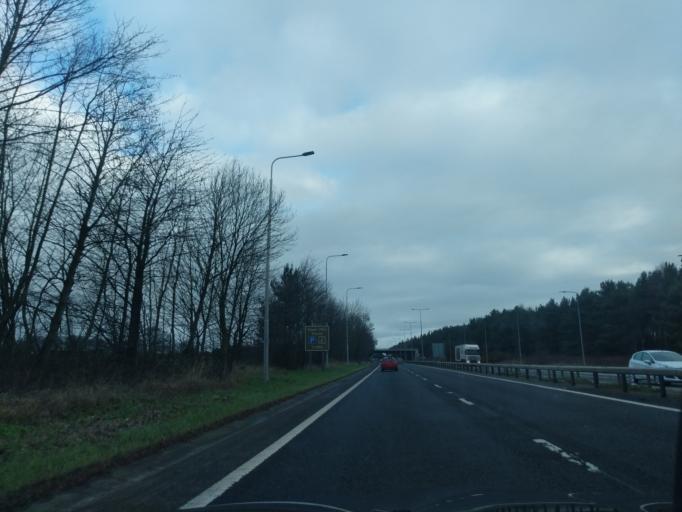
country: GB
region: England
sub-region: Newcastle upon Tyne
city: Hazlerigg
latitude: 55.0666
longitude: -1.6383
